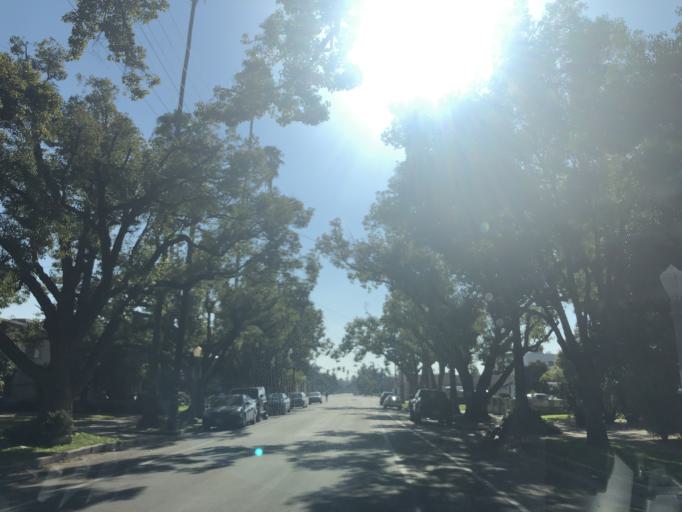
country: US
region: California
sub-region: Los Angeles County
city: East Pasadena
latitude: 34.1475
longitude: -118.1158
